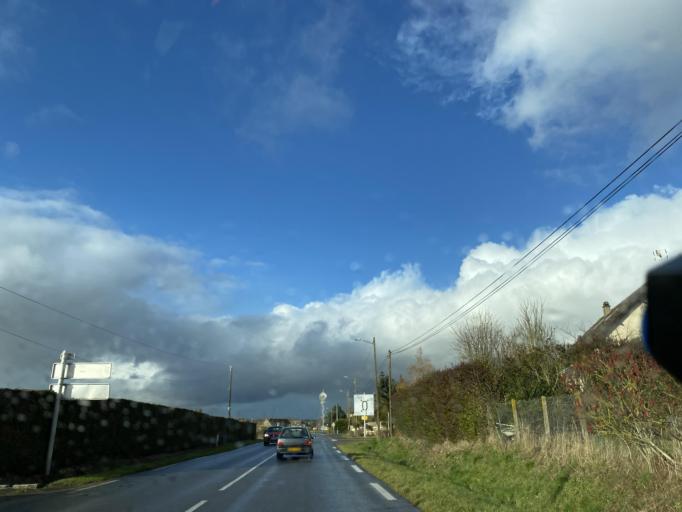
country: FR
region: Centre
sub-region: Departement d'Eure-et-Loir
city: Brezolles
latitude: 48.6876
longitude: 1.0819
